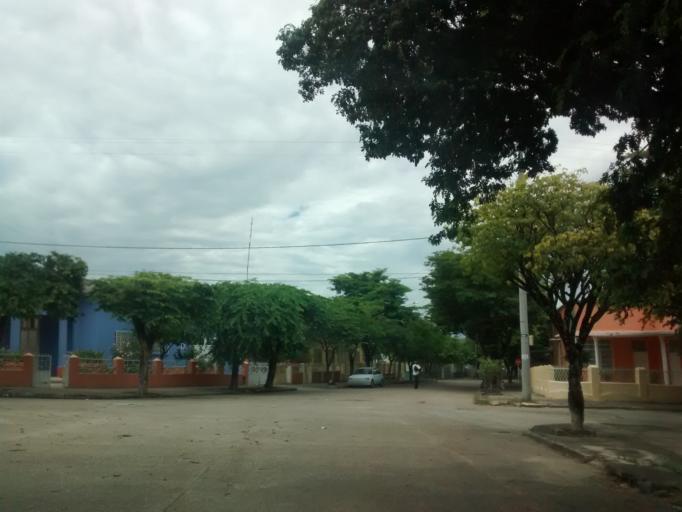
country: CO
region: Cundinamarca
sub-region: Girardot
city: Girardot City
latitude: 4.3026
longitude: -74.8101
